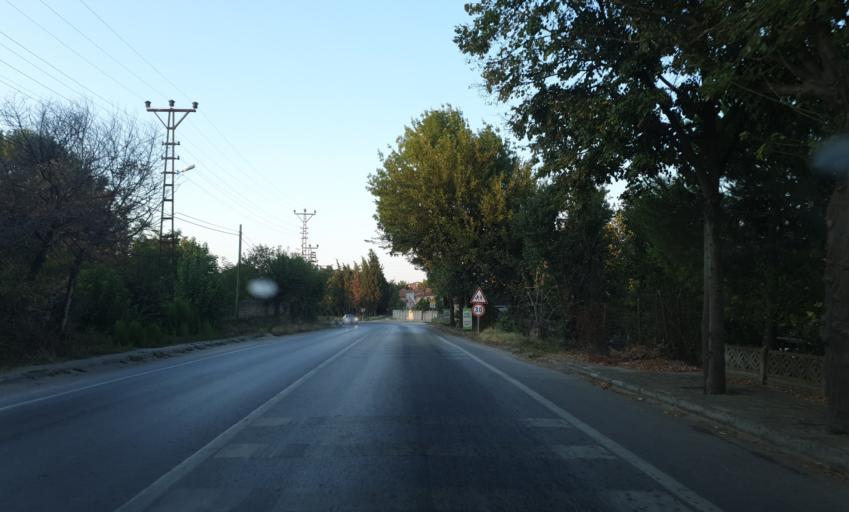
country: TR
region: Kirklareli
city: Luleburgaz
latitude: 41.4570
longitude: 27.3872
